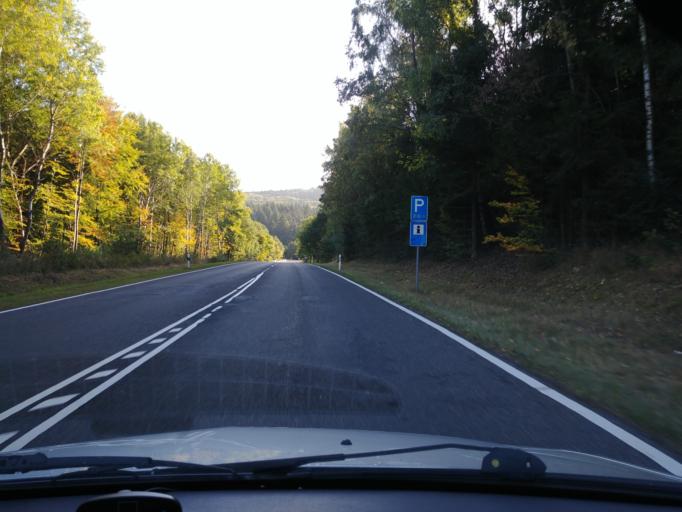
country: DE
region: Hesse
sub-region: Regierungsbezirk Darmstadt
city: Waldems
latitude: 50.2808
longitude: 8.3616
